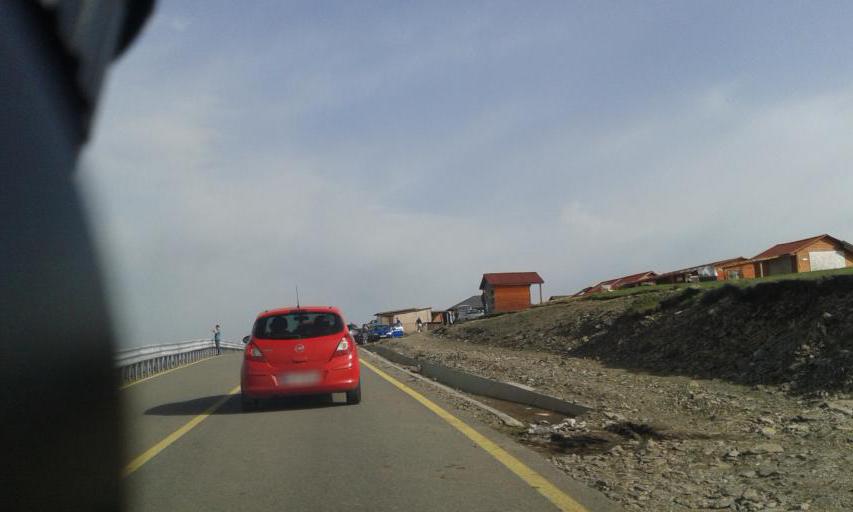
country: RO
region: Gorj
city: Novaci-Straini
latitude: 45.3654
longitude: 23.6506
